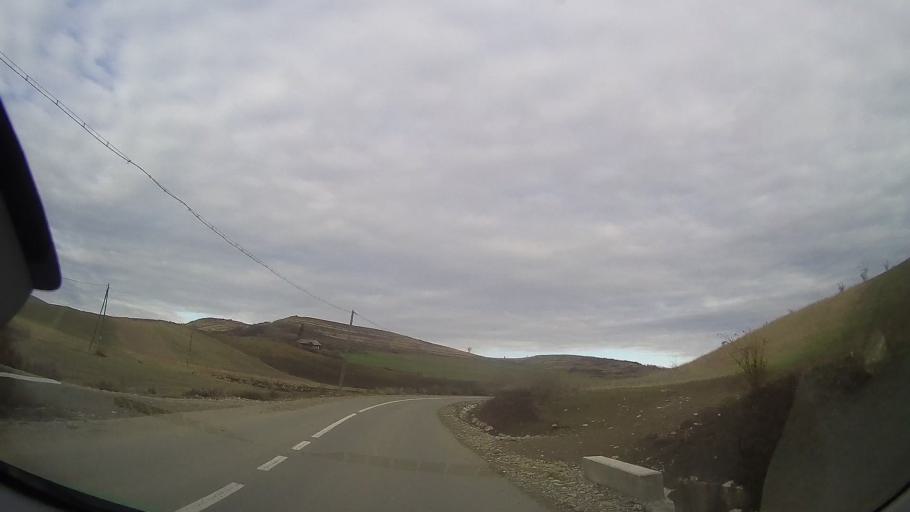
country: RO
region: Bistrita-Nasaud
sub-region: Comuna Silvasu de Campie
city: Silvasu de Campie
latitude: 46.8180
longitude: 24.2967
